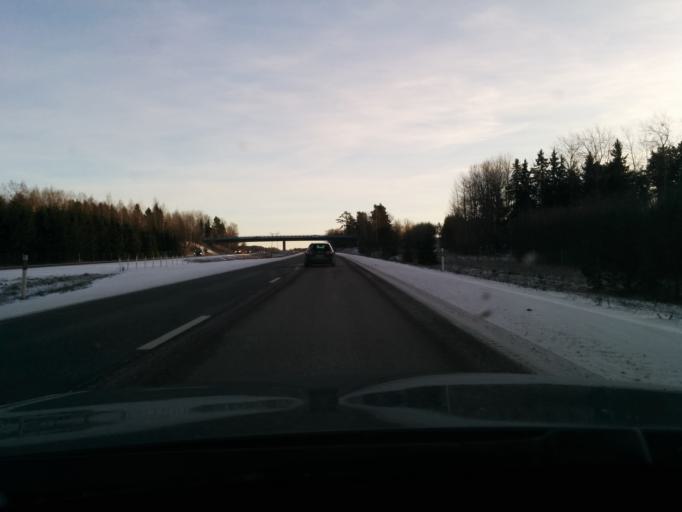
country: SE
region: Uppsala
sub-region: Habo Kommun
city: Balsta
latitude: 59.6007
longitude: 17.4402
